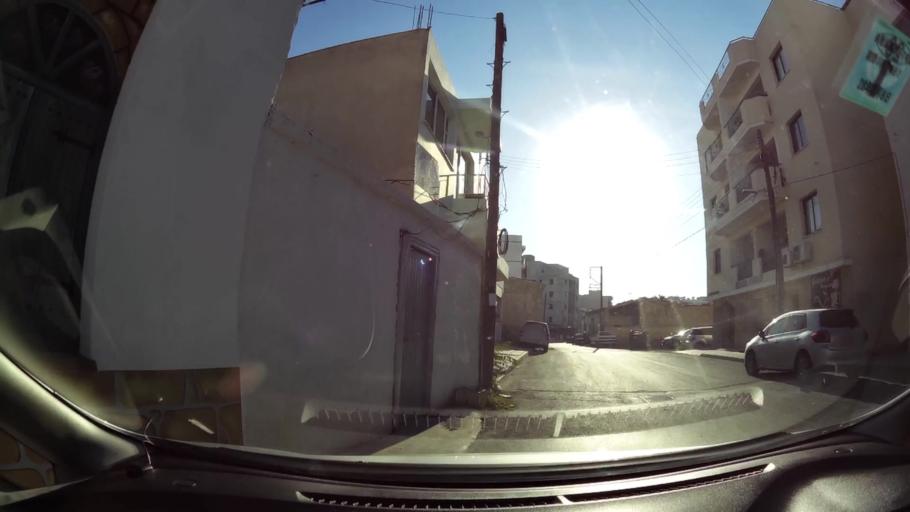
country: CY
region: Larnaka
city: Larnaca
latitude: 34.9211
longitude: 33.6205
